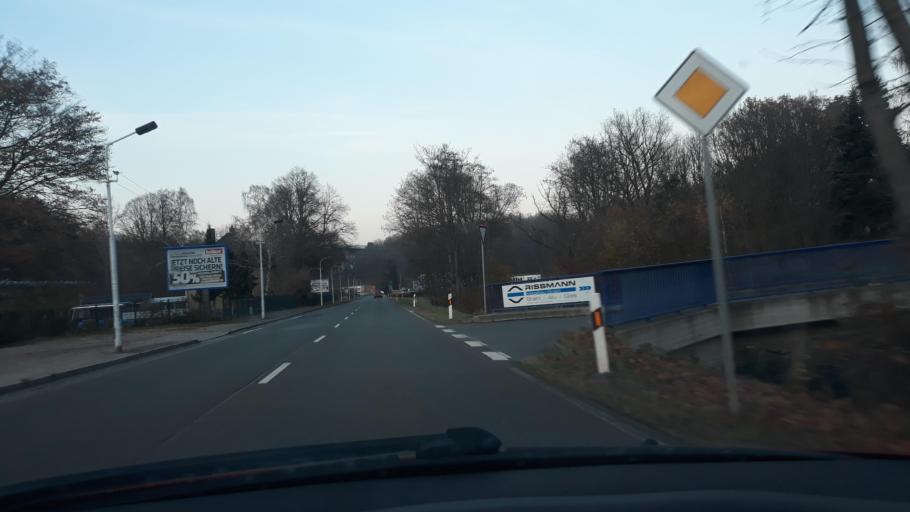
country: DE
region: Saxony
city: Wilkau-Hasslau
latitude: 50.6658
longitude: 12.5242
